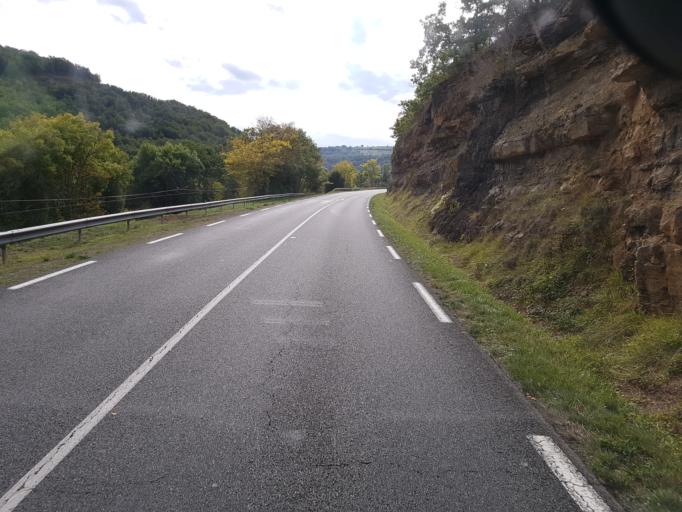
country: FR
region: Midi-Pyrenees
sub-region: Departement de l'Aveyron
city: Saint-Georges-de-Luzencon
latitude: 44.0425
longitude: 2.9679
